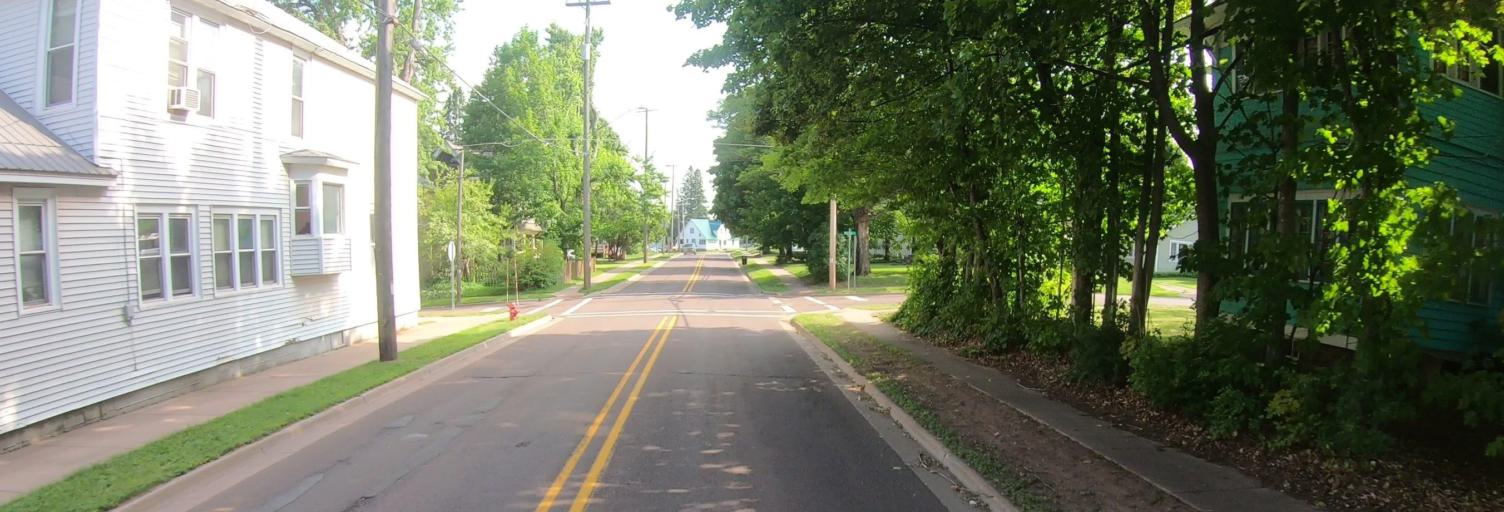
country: US
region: Michigan
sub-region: Gogebic County
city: Ironwood
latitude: 46.4580
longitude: -90.1727
